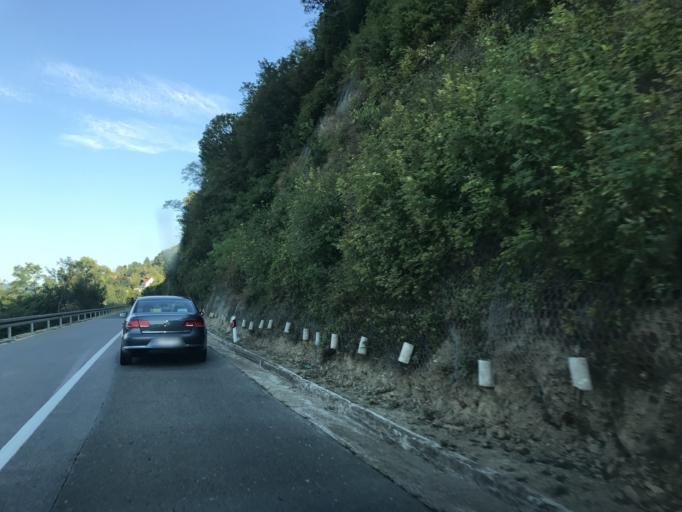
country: RO
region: Mehedinti
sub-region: Comuna Svinita
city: Svinita
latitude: 44.4746
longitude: 22.1064
